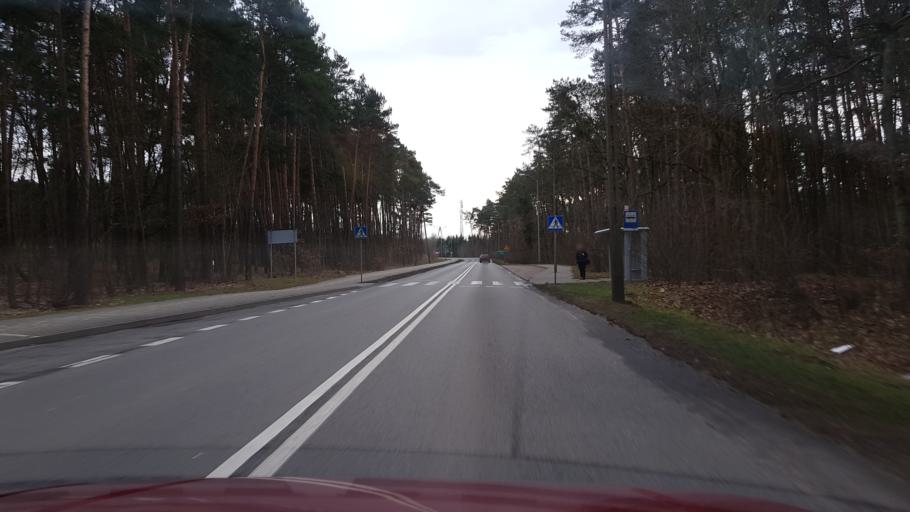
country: PL
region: West Pomeranian Voivodeship
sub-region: Powiat policki
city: Dobra
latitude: 53.5036
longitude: 14.4777
